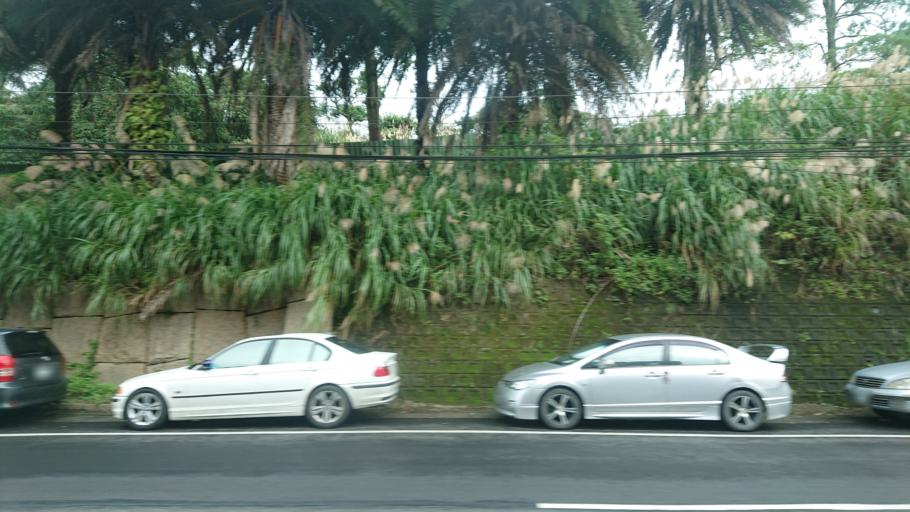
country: TW
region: Taiwan
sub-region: Taoyuan
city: Taoyuan
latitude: 24.9386
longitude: 121.3956
